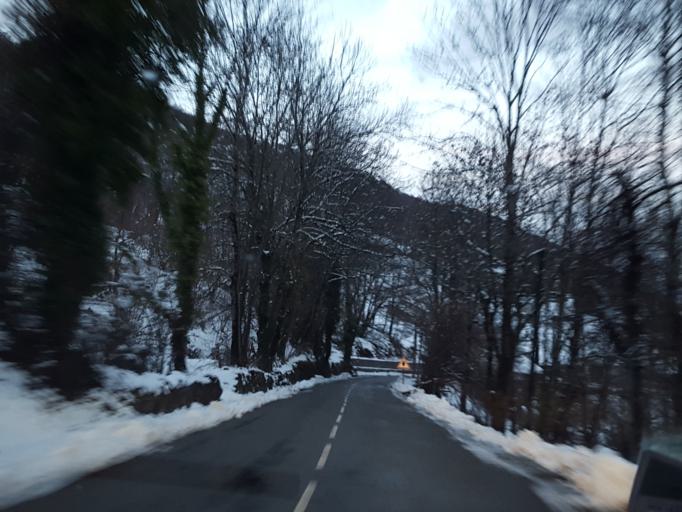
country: FR
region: Midi-Pyrenees
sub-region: Departement de l'Ariege
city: Tarascon-sur-Ariege
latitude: 42.8949
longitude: 1.4733
